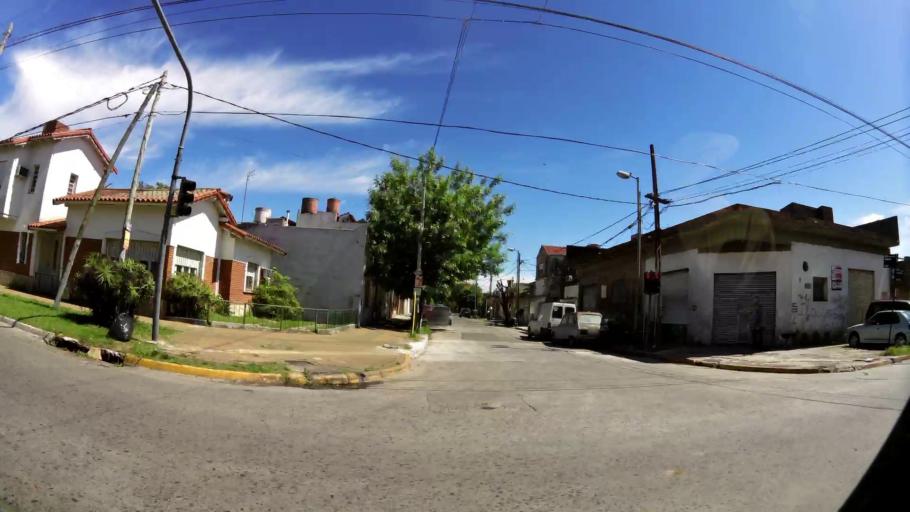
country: AR
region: Buenos Aires
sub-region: Partido de Quilmes
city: Quilmes
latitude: -34.7118
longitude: -58.2649
